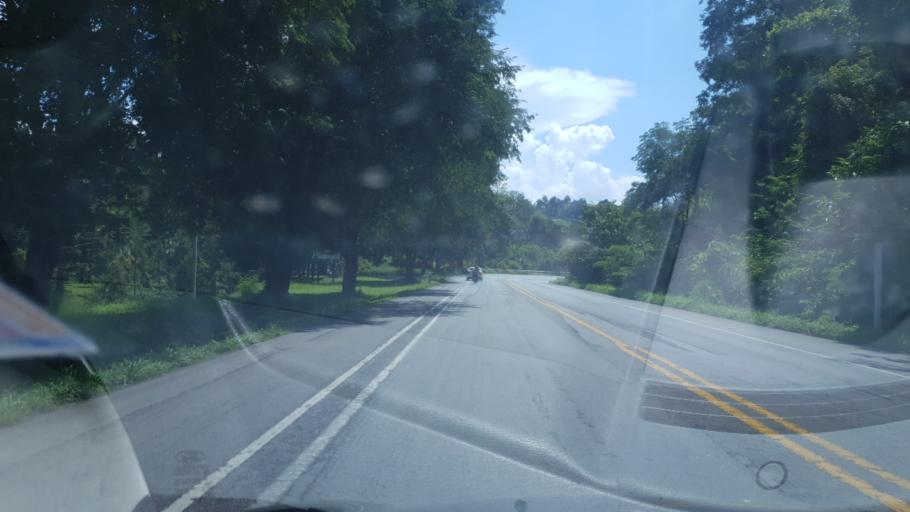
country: TH
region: Chiang Rai
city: Mae Suai
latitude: 19.6967
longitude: 99.5814
